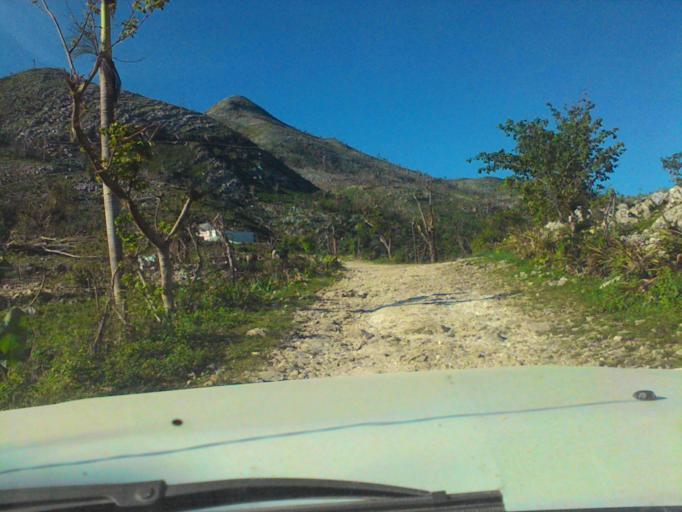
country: HT
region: Grandans
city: Jeremie
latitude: 18.5016
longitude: -74.0932
